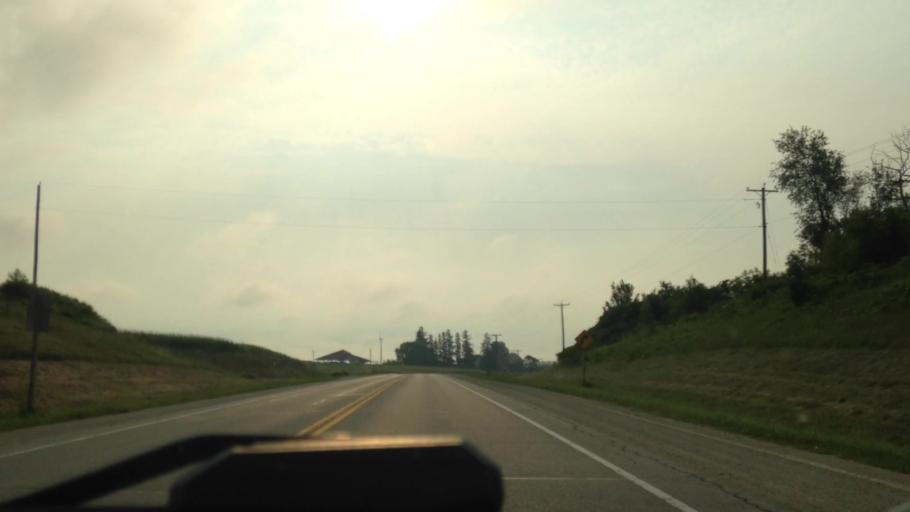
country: US
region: Wisconsin
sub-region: Dodge County
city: Mayville
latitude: 43.4431
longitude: -88.4973
